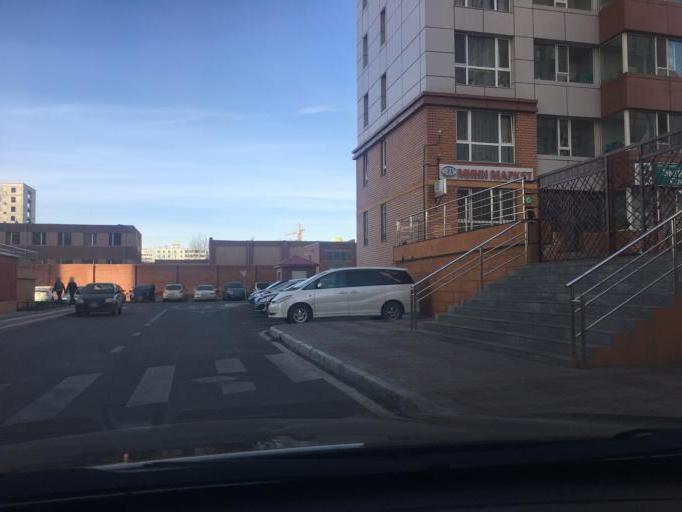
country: MN
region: Ulaanbaatar
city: Ulaanbaatar
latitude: 47.9061
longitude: 106.8969
